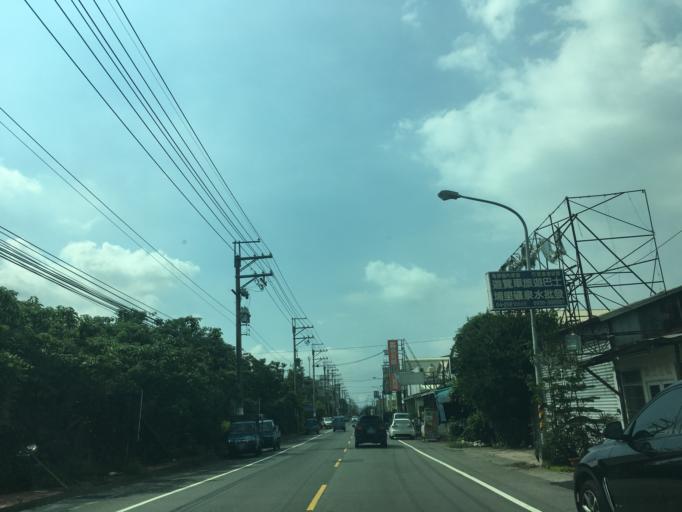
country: TW
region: Taiwan
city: Fengyuan
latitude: 24.2504
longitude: 120.8089
